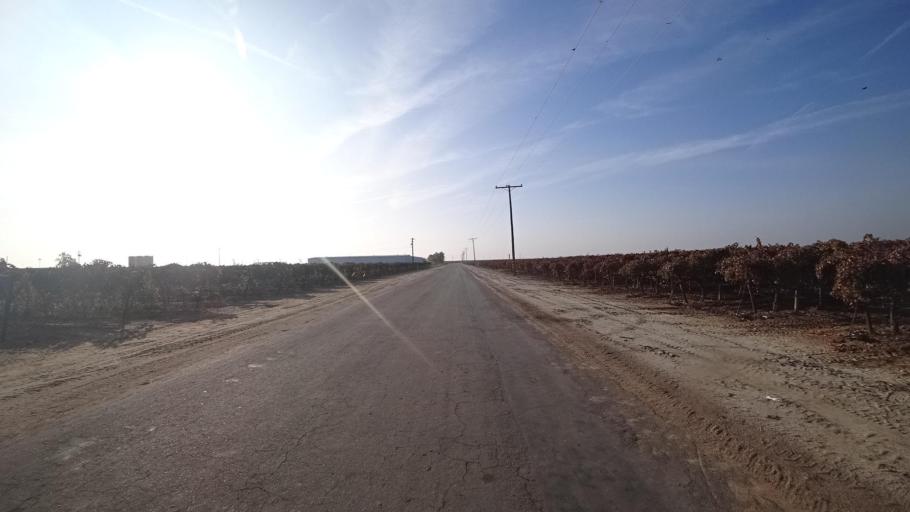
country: US
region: California
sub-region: Kern County
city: McFarland
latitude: 35.6796
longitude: -119.1871
